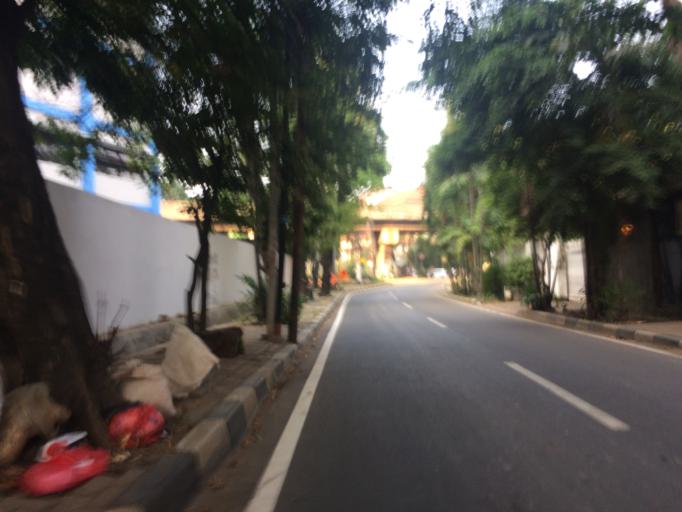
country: ID
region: Jakarta Raya
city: Jakarta
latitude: -6.2021
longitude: 106.8429
